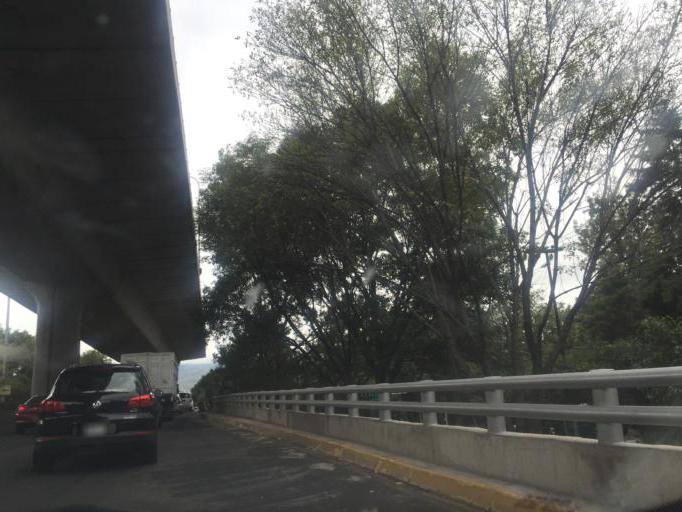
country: MX
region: Mexico City
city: Tlalpan
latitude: 19.2870
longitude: -99.1566
